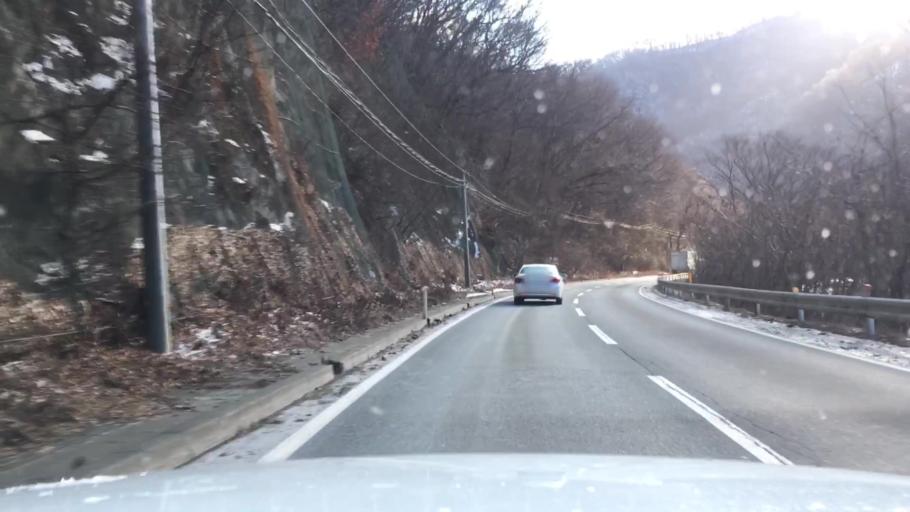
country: JP
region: Iwate
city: Tono
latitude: 39.6193
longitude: 141.4950
